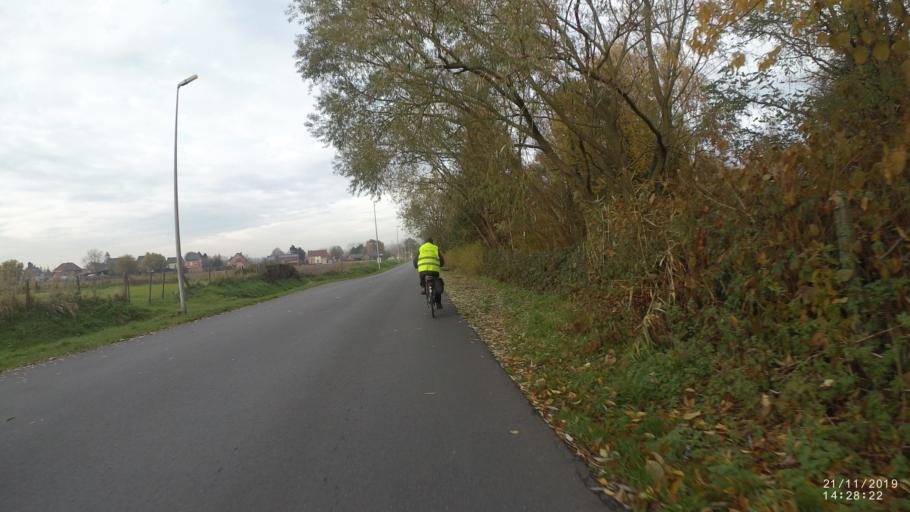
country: BE
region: Flanders
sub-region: Provincie Limburg
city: Alken
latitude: 50.8936
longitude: 5.3041
